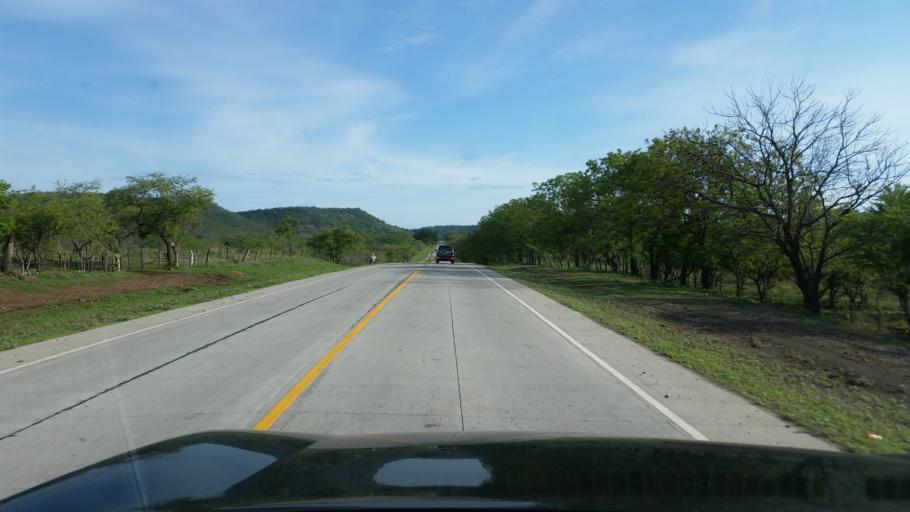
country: NI
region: Leon
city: Nagarote
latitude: 12.1369
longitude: -86.6480
